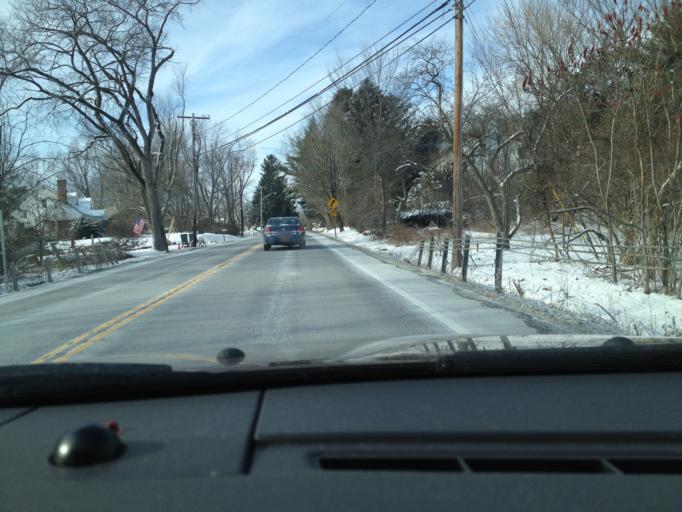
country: US
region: New York
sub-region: Rensselaer County
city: Wynantskill
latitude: 42.6516
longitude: -73.6716
